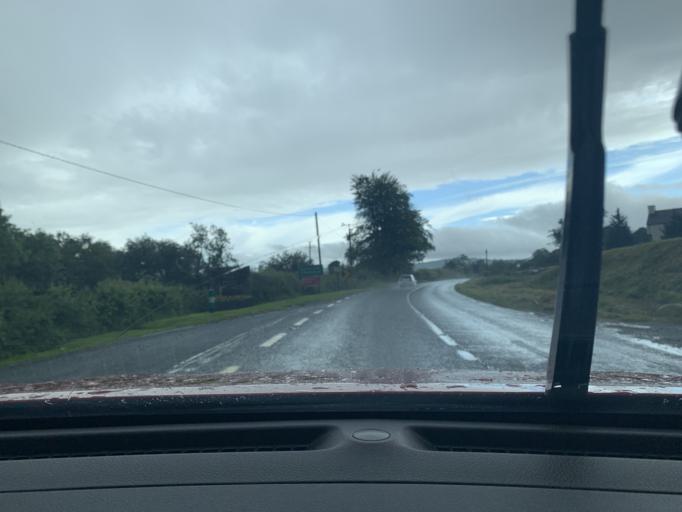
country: IE
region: Ulster
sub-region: County Donegal
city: Ballybofey
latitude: 54.8149
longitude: -7.7586
